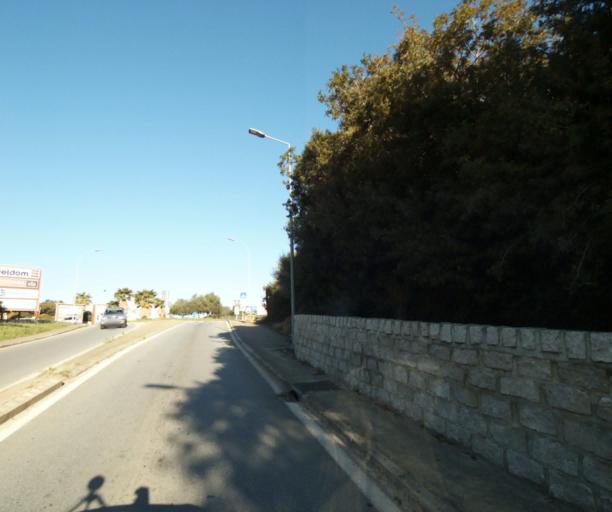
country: FR
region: Corsica
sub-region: Departement de la Corse-du-Sud
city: Propriano
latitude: 41.6691
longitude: 8.9194
